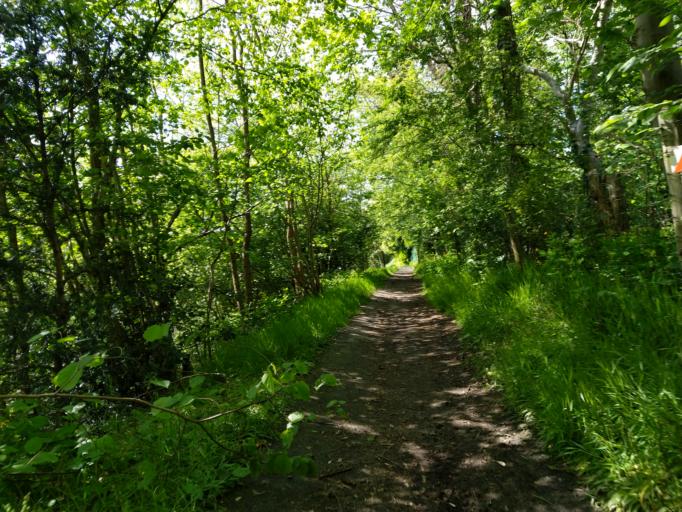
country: BE
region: Wallonia
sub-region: Province du Hainaut
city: Mons
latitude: 50.4814
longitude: 3.9367
